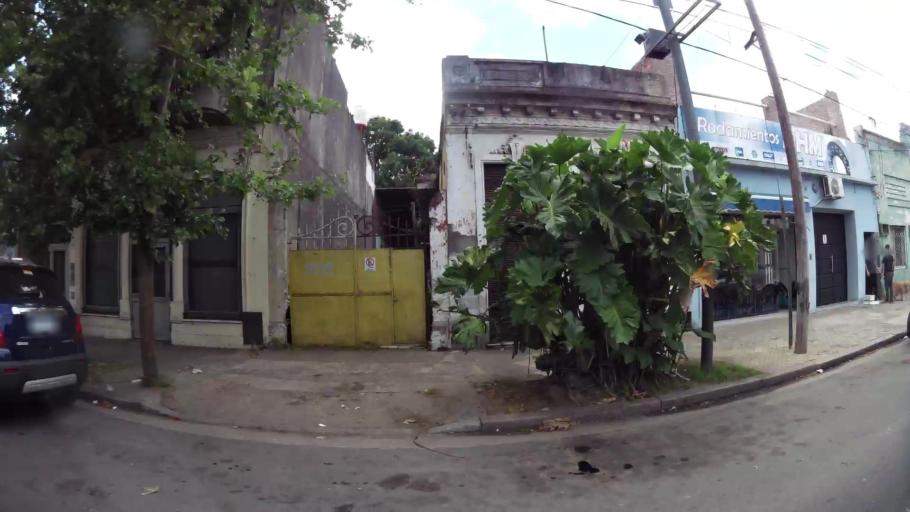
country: AR
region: Santa Fe
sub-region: Departamento de Rosario
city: Rosario
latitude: -32.9686
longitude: -60.6421
